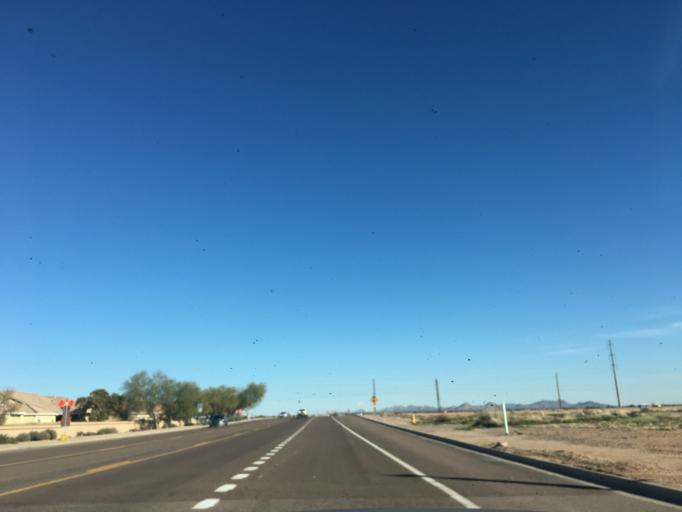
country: US
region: Arizona
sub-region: Pinal County
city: Maricopa
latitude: 33.0436
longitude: -111.9992
